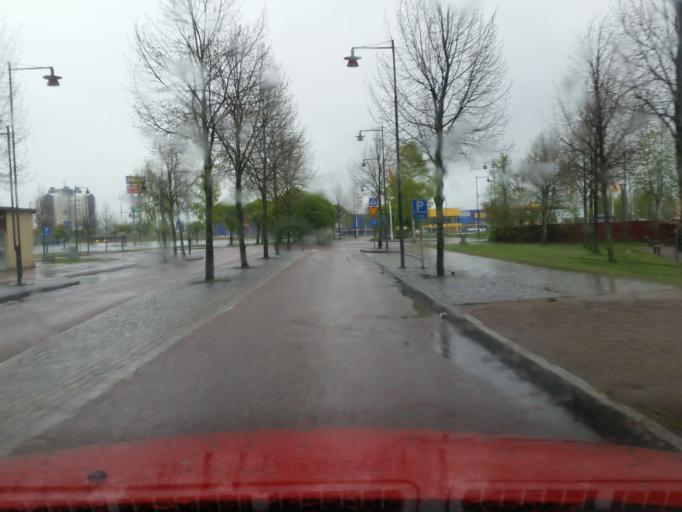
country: SE
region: Dalarna
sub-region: Borlange Kommun
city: Borlaenge
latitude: 60.4826
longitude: 15.4130
